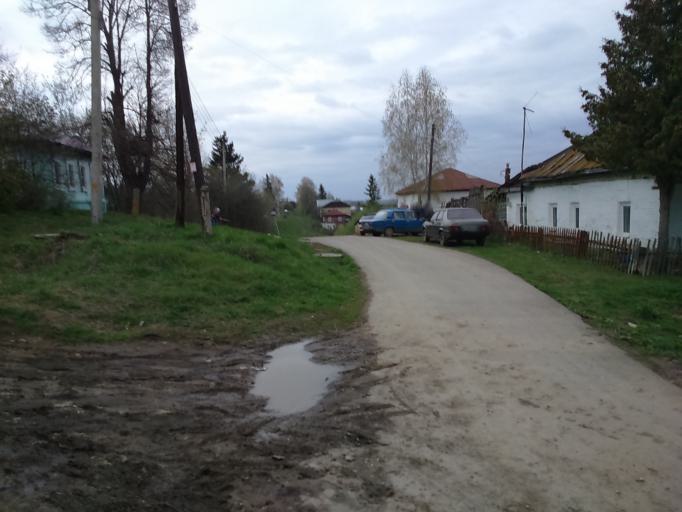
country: RU
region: Tula
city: Krapivna
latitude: 53.9425
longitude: 37.1601
